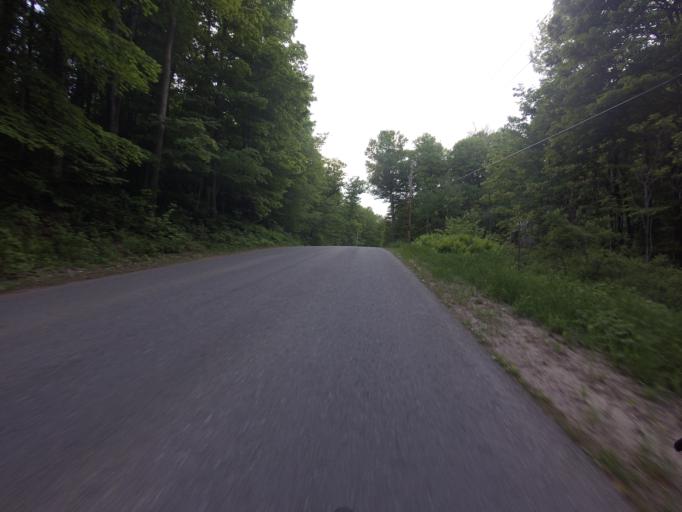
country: US
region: New York
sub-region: St. Lawrence County
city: Gouverneur
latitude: 44.1574
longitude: -75.3759
